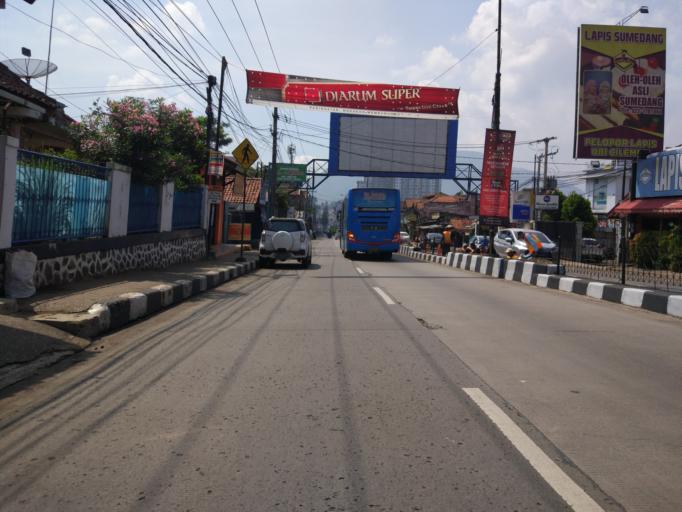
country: ID
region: West Java
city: Cileunyi
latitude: -6.9371
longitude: 107.7602
